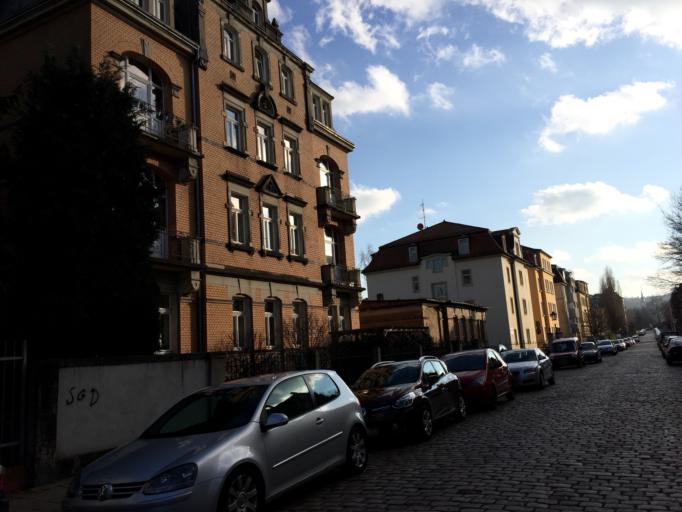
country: DE
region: Saxony
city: Dresden
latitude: 51.0381
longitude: 13.7030
